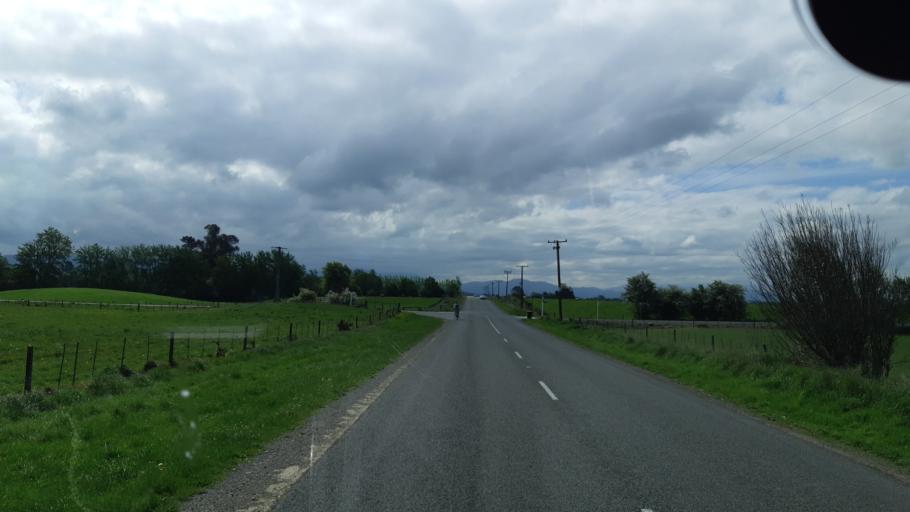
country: NZ
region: Canterbury
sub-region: Timaru District
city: Pleasant Point
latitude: -44.1731
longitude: 171.2202
